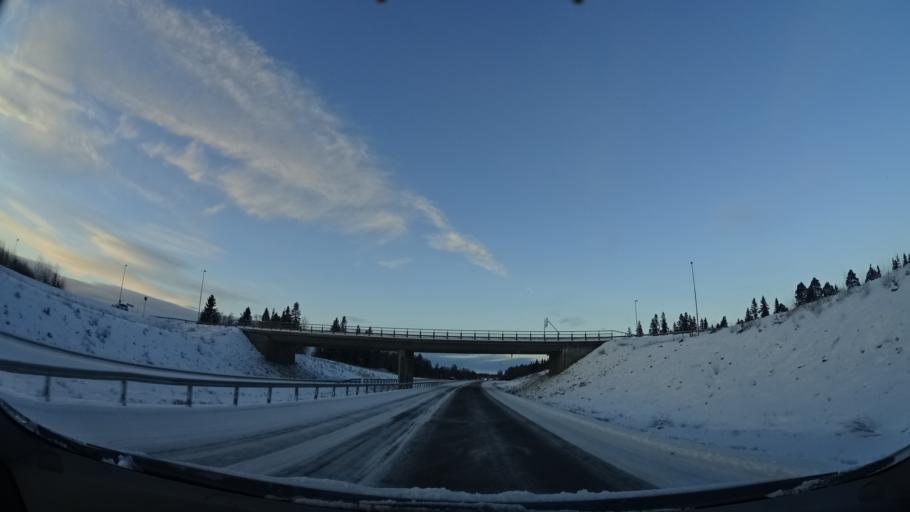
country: SE
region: Vaesterbotten
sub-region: Skelleftea Kommun
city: Kage
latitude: 64.8285
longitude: 21.0159
